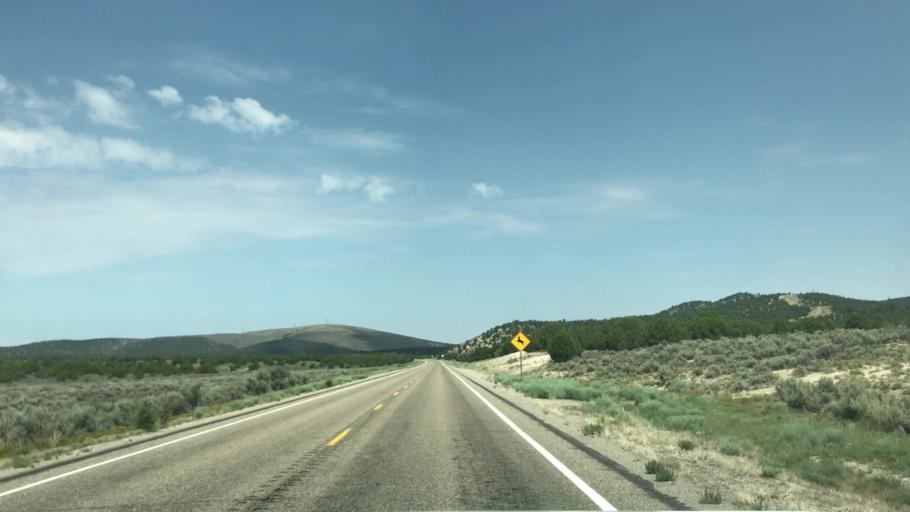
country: US
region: Nevada
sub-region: White Pine County
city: Ely
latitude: 39.3762
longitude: -115.0621
